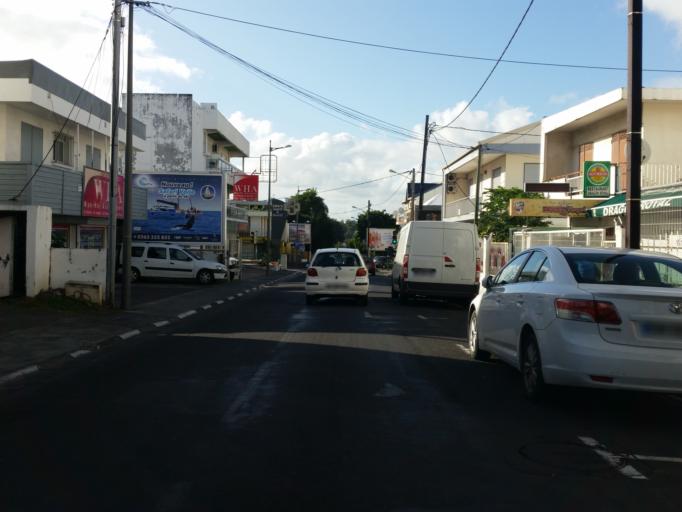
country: RE
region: Reunion
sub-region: Reunion
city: Saint-Denis
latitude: -20.8871
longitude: 55.4623
